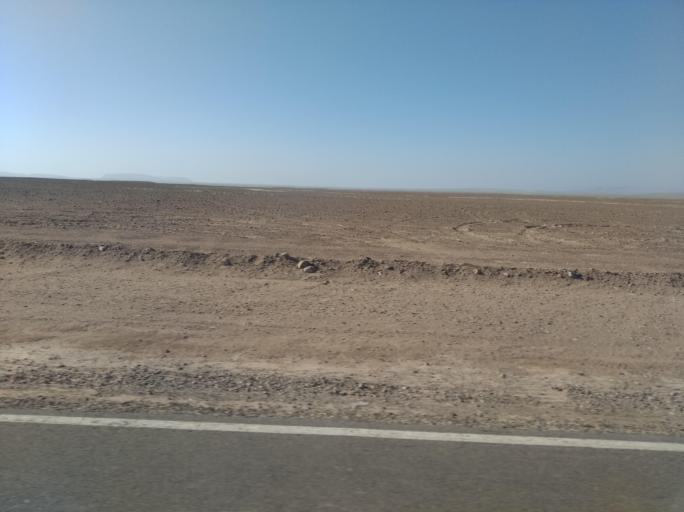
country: CL
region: Atacama
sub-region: Provincia de Copiapo
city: Copiapo
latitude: -27.3167
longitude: -70.8597
